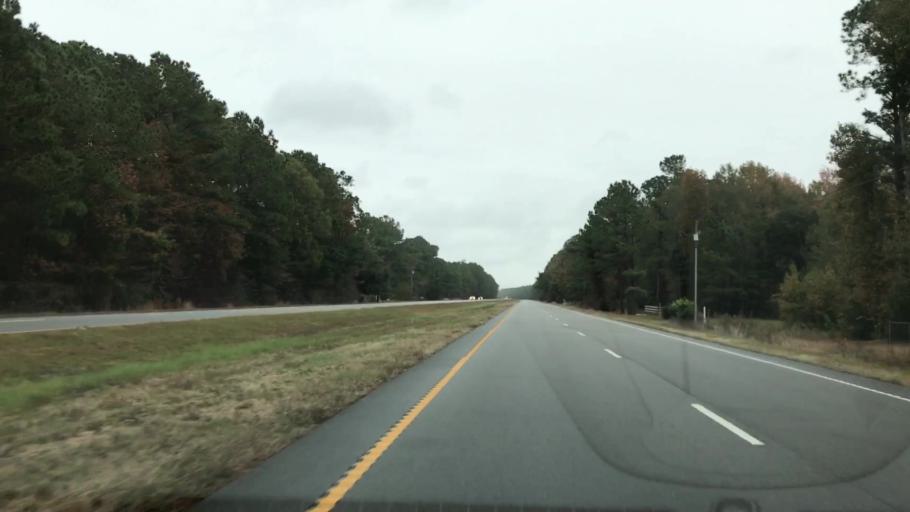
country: US
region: South Carolina
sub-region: Charleston County
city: Awendaw
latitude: 33.1143
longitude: -79.4576
